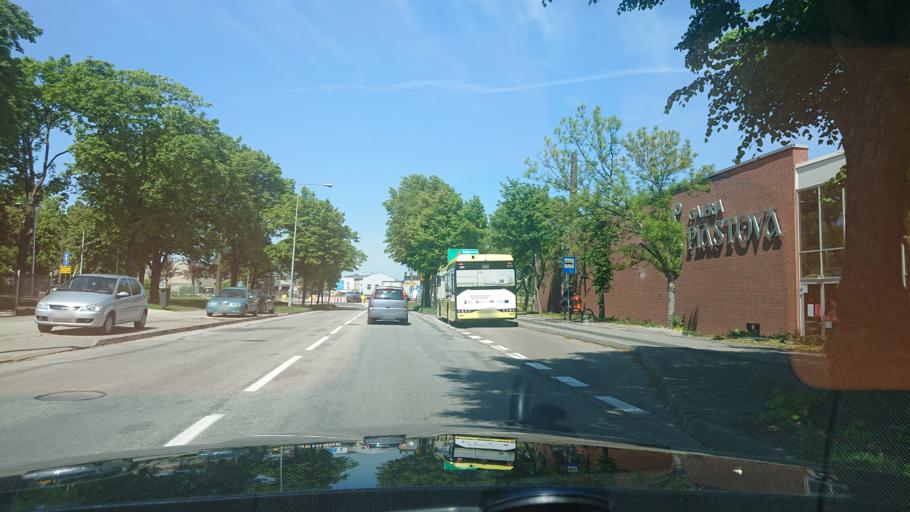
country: PL
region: Greater Poland Voivodeship
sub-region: Powiat gnieznienski
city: Gniezno
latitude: 52.5262
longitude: 17.5986
